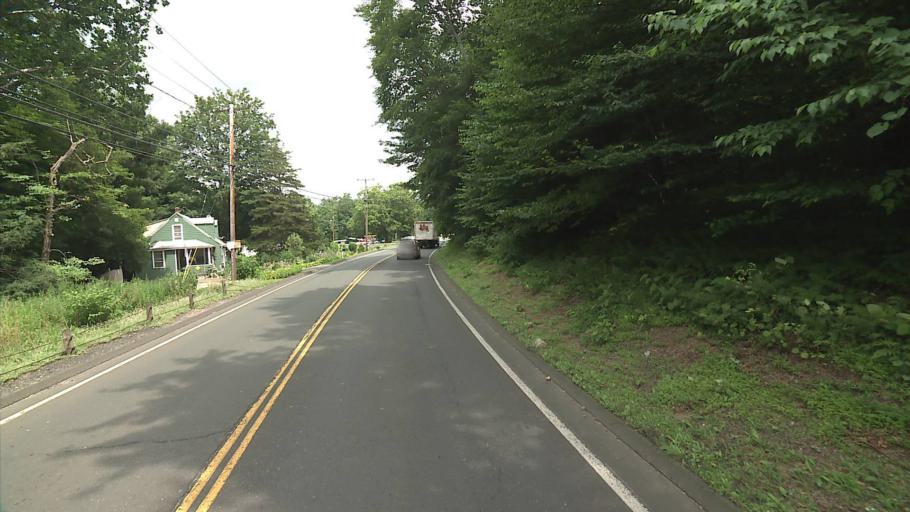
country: US
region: Connecticut
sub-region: New Haven County
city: Seymour
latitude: 41.3985
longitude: -73.0531
